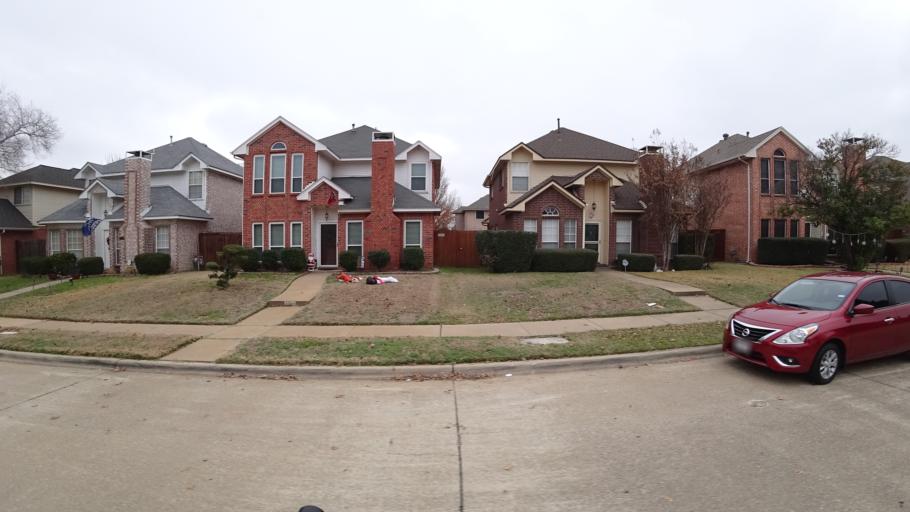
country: US
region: Texas
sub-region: Denton County
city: Lewisville
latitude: 33.0247
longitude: -97.0307
